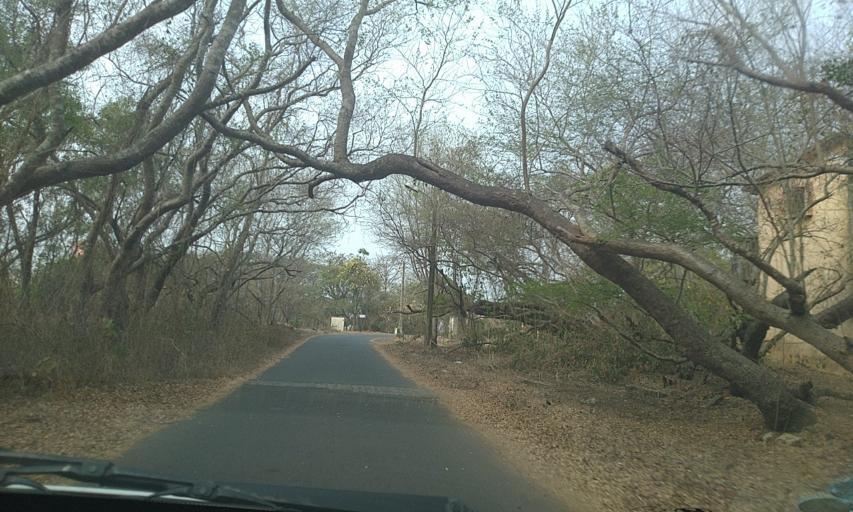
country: IN
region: Goa
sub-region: North Goa
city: Taleigao
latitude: 15.4552
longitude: 73.8389
